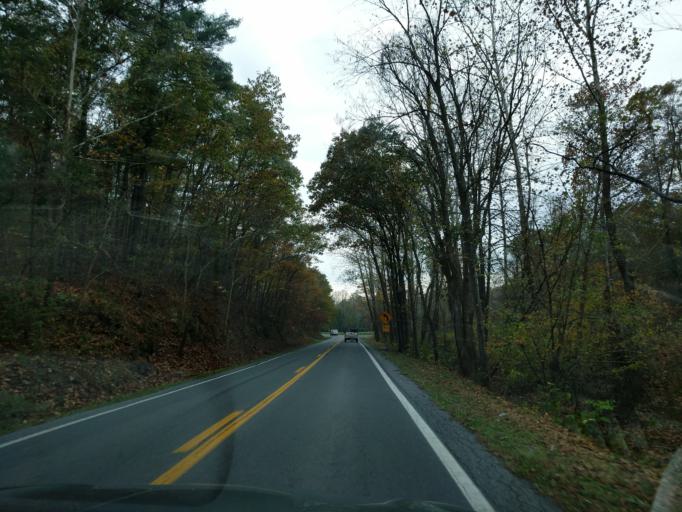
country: US
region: West Virginia
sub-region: Berkeley County
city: Inwood
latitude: 39.3852
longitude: -78.1378
